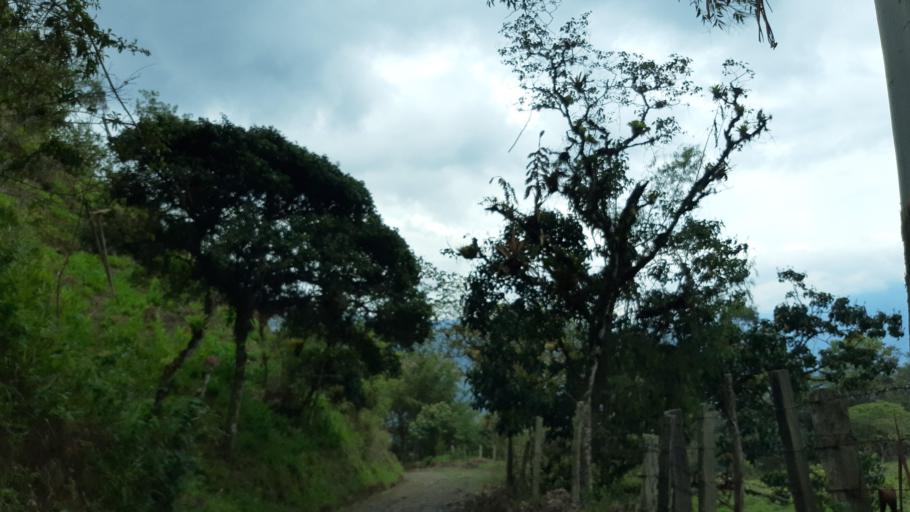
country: CO
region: Boyaca
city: Garagoa
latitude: 5.0530
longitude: -73.3479
